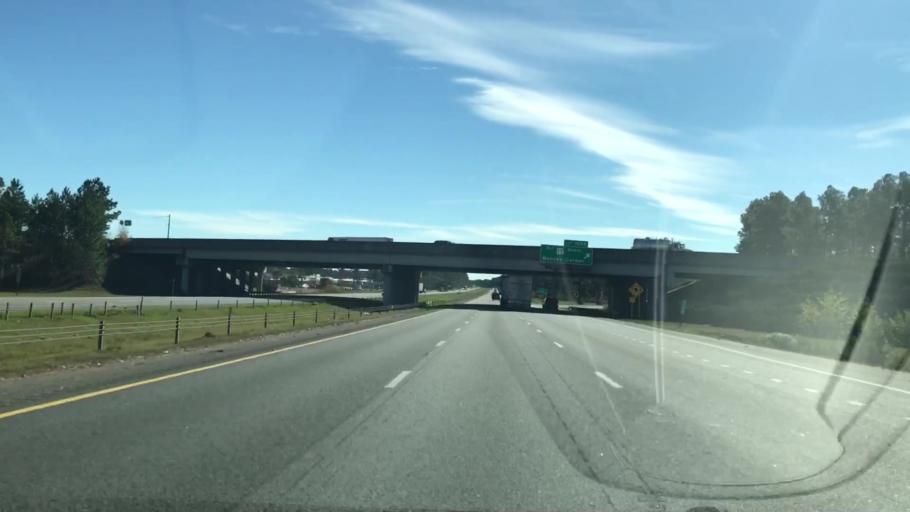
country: US
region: South Carolina
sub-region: Berkeley County
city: Sangaree
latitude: 33.0390
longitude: -80.1497
